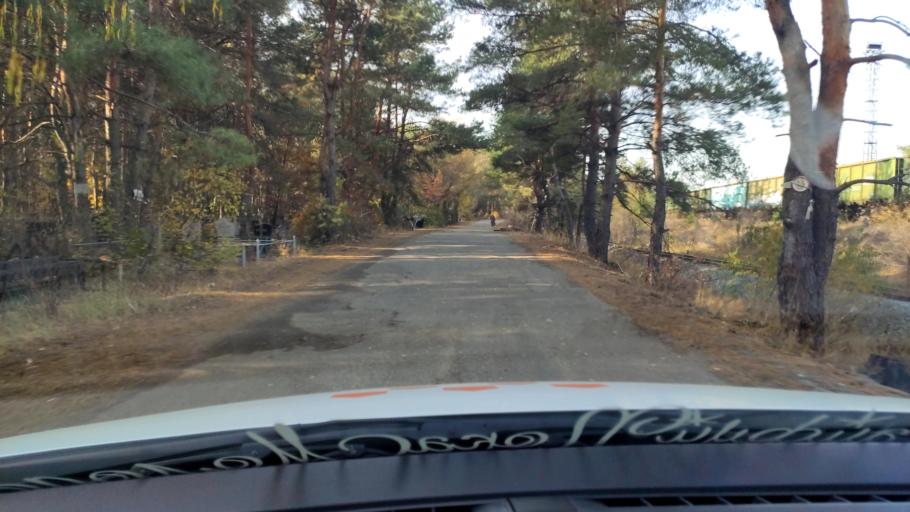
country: RU
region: Voronezj
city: Pridonskoy
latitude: 51.6695
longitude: 39.1007
